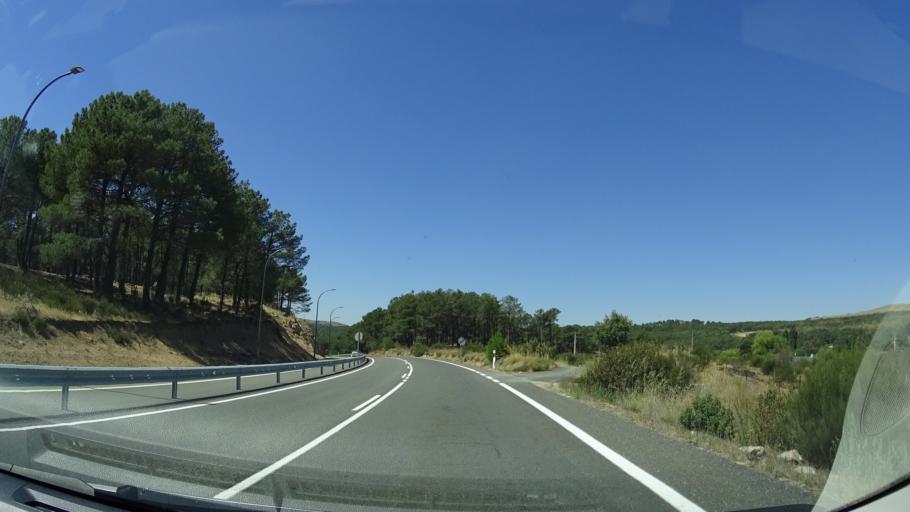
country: ES
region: Castille and Leon
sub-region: Provincia de Avila
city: Las Navas del Marques
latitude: 40.5945
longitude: -4.3575
